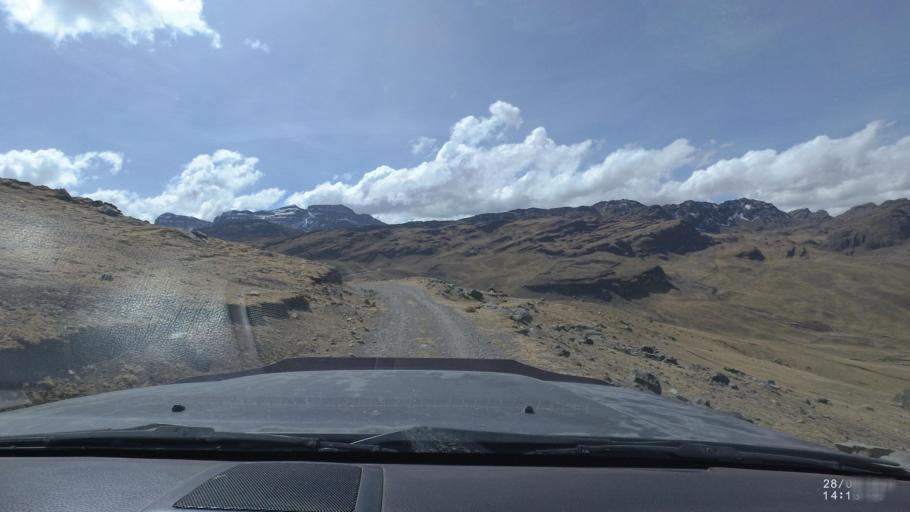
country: BO
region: Cochabamba
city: Sipe Sipe
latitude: -17.2580
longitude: -66.3869
